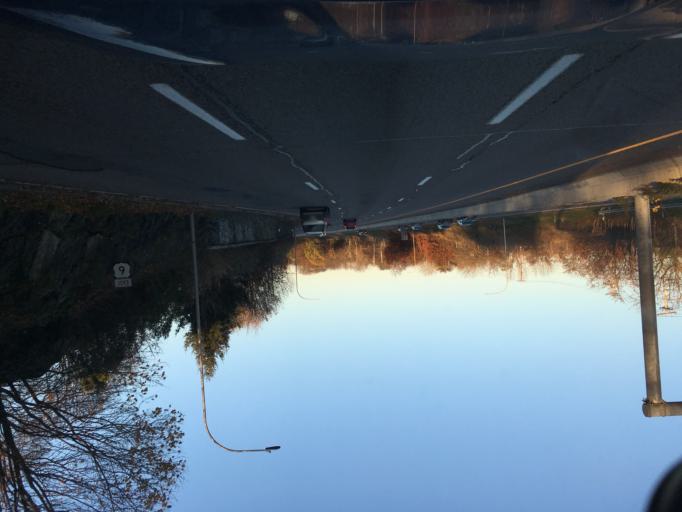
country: US
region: Rhode Island
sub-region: Providence County
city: North Providence
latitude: 41.8228
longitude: -71.4655
